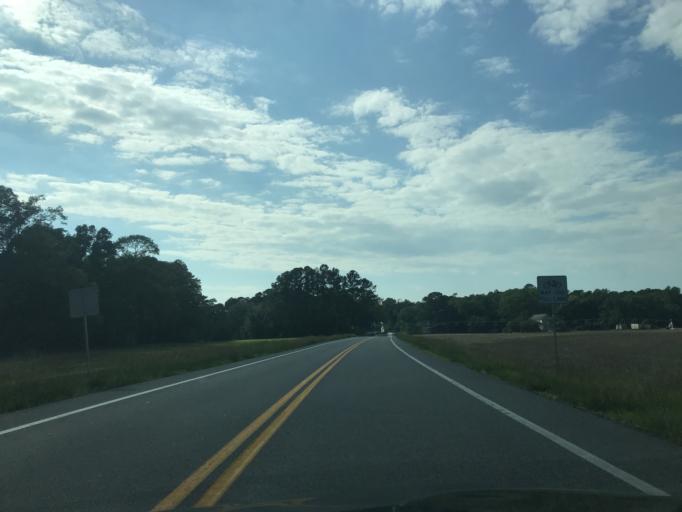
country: US
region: Maryland
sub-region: Wicomico County
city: Hebron
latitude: 38.4614
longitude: -75.7044
